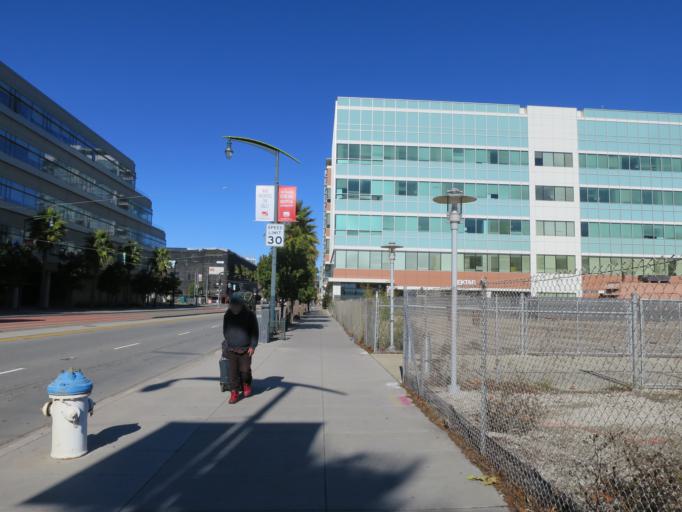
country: US
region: California
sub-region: San Francisco County
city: San Francisco
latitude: 37.7697
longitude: -122.3892
